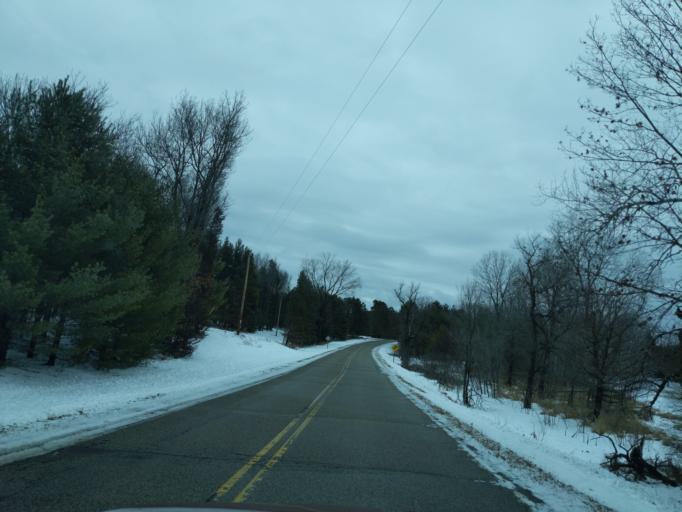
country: US
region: Wisconsin
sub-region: Marquette County
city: Montello
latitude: 43.9092
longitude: -89.3683
